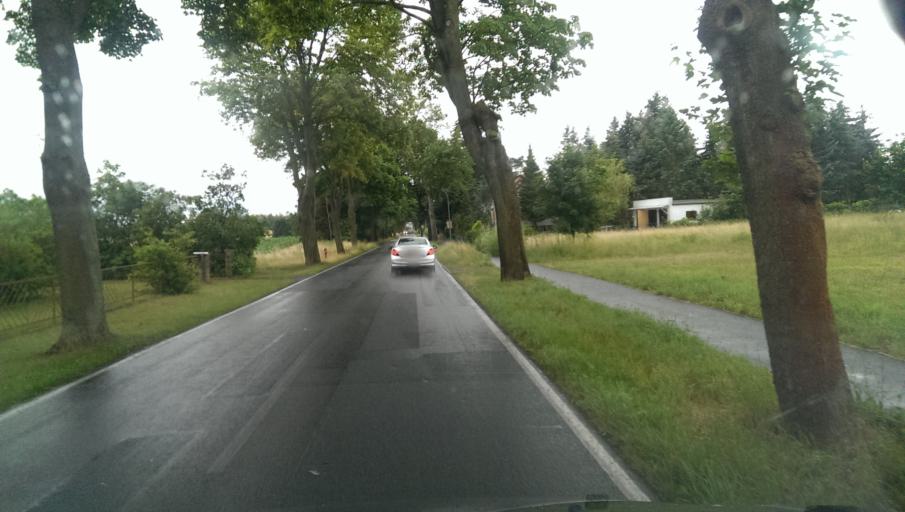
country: DE
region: Brandenburg
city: Gross Kreutz
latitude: 52.4001
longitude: 12.7139
